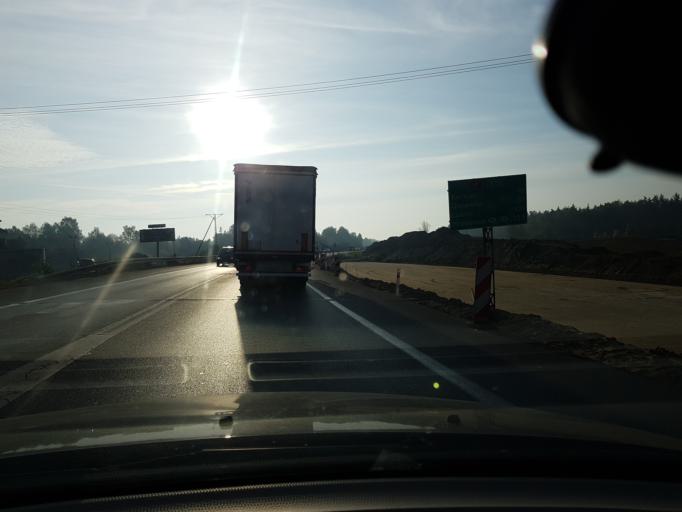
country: PL
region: Masovian Voivodeship
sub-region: Powiat otwocki
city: Jozefow
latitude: 52.1651
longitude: 21.2975
